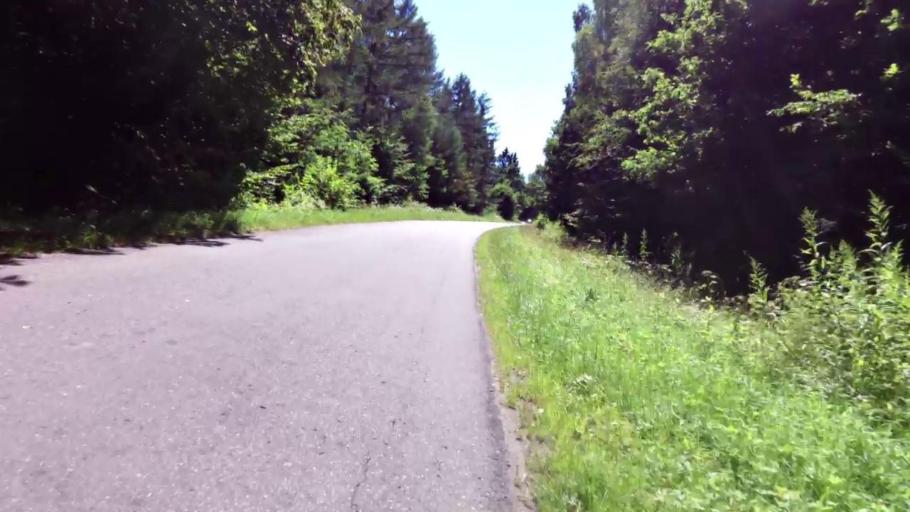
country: PL
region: West Pomeranian Voivodeship
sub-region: Powiat szczecinecki
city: Bialy Bor
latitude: 53.9392
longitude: 16.8540
